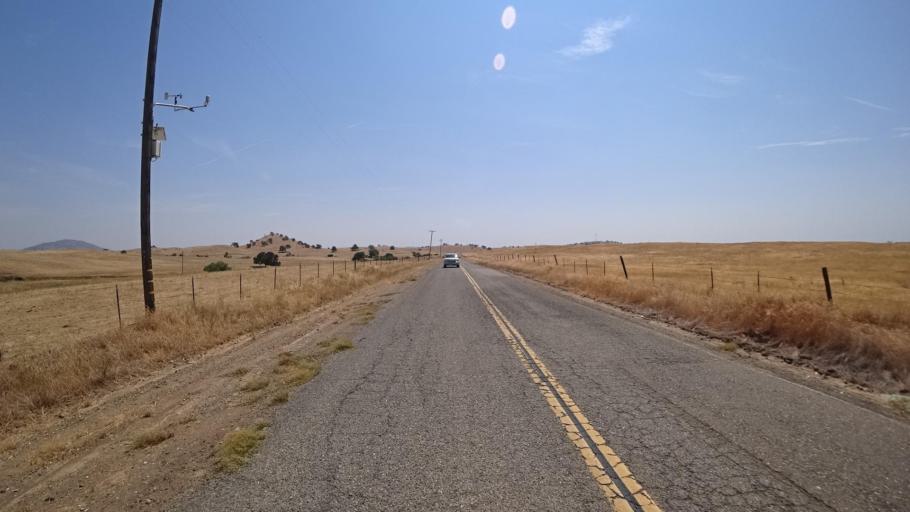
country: US
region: California
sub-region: Mariposa County
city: Mariposa
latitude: 37.5328
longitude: -120.2076
